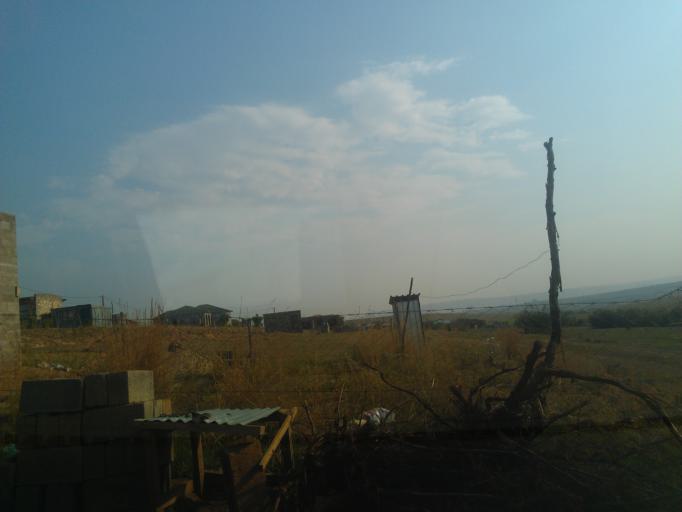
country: LS
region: Berea
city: Teyateyaneng
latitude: -29.1325
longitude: 27.7635
